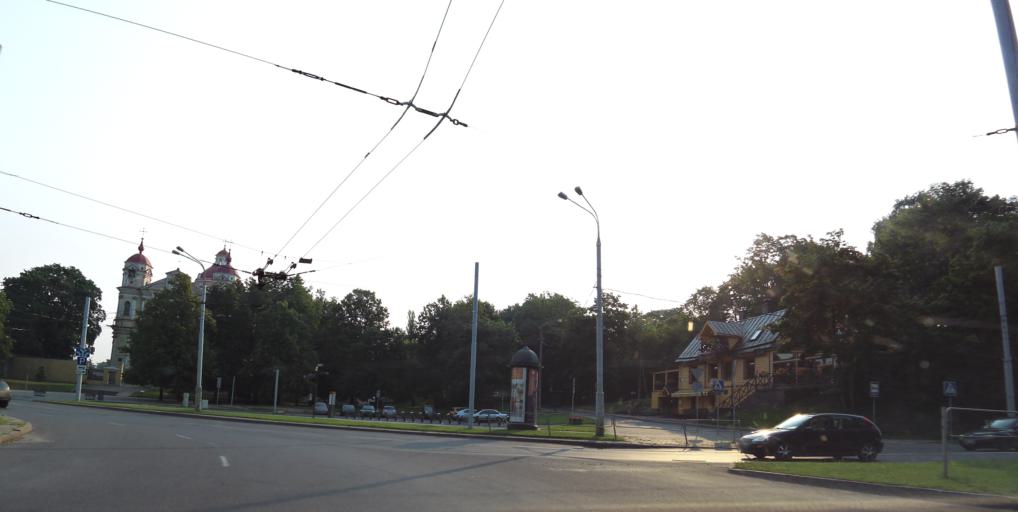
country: LT
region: Vilnius County
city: Rasos
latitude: 54.6931
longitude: 25.3044
